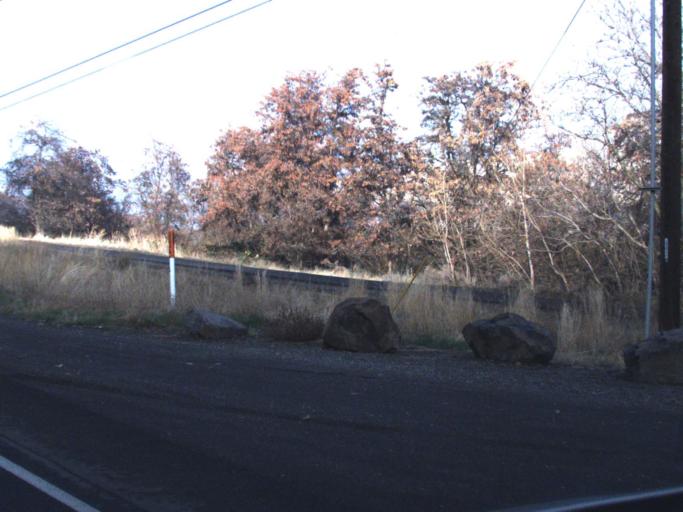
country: US
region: Washington
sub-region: Asotin County
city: Asotin
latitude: 46.3436
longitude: -117.0580
